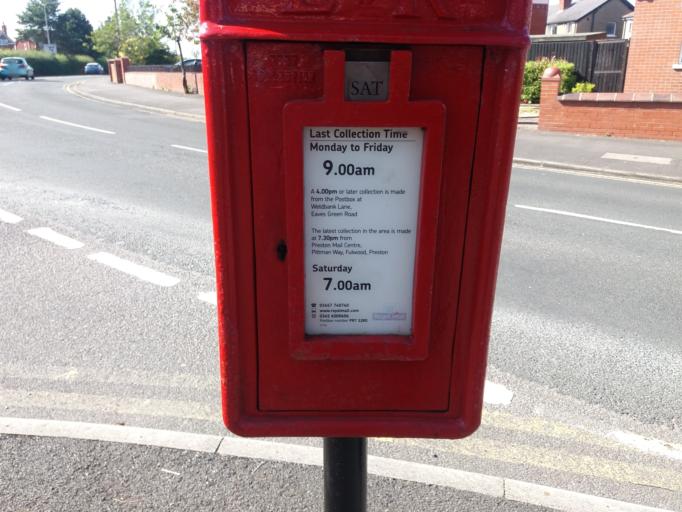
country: GB
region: England
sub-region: Lancashire
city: Chorley
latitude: 53.6395
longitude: -2.6285
